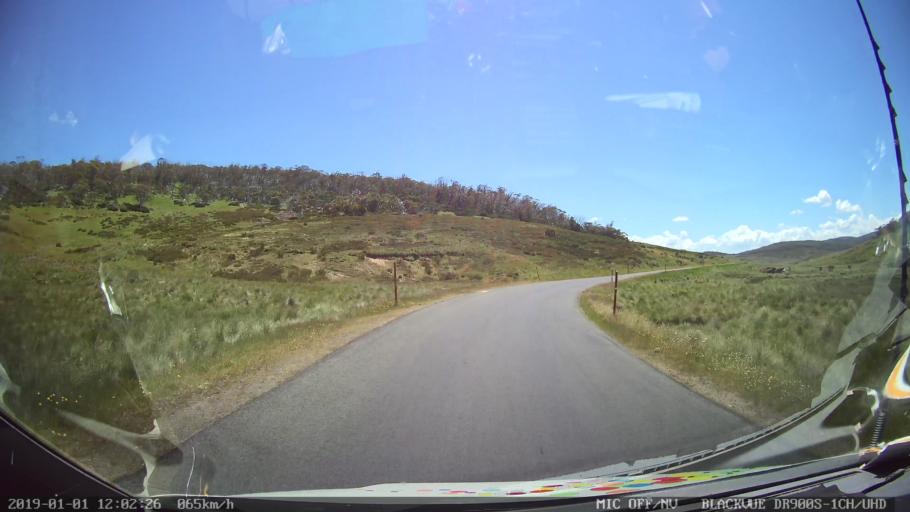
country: AU
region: New South Wales
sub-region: Snowy River
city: Jindabyne
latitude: -35.8725
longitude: 148.4767
